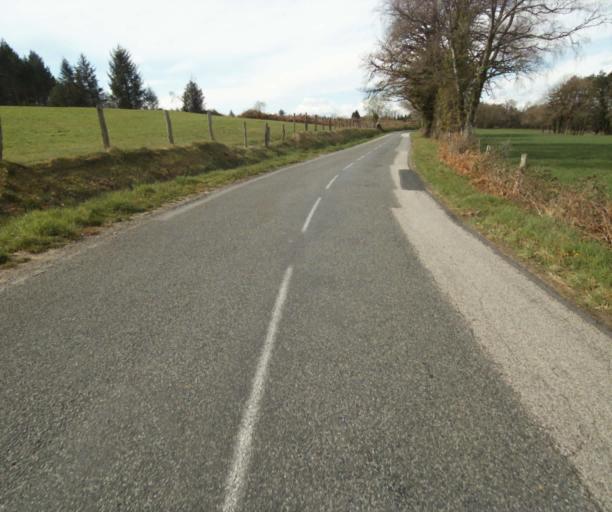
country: FR
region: Limousin
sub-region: Departement de la Correze
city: Correze
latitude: 45.3550
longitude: 1.9100
